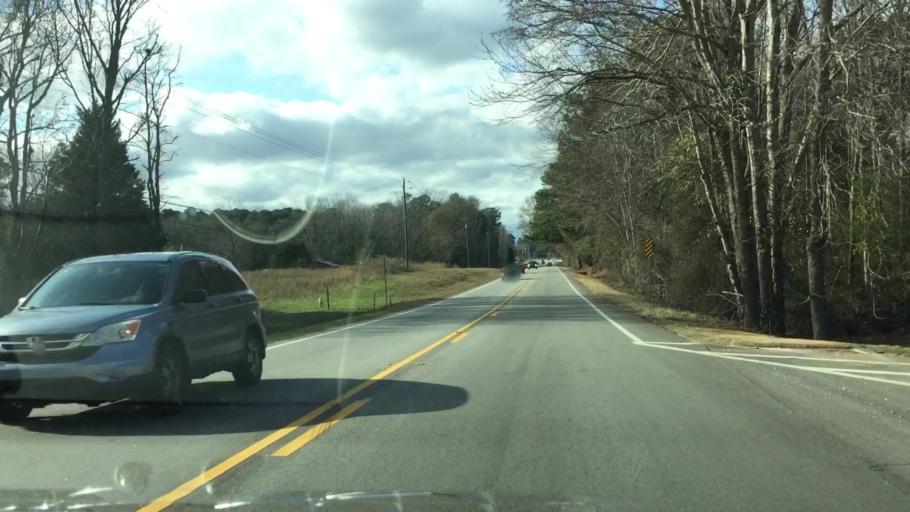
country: US
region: Georgia
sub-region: Henry County
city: McDonough
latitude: 33.4273
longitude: -84.0820
